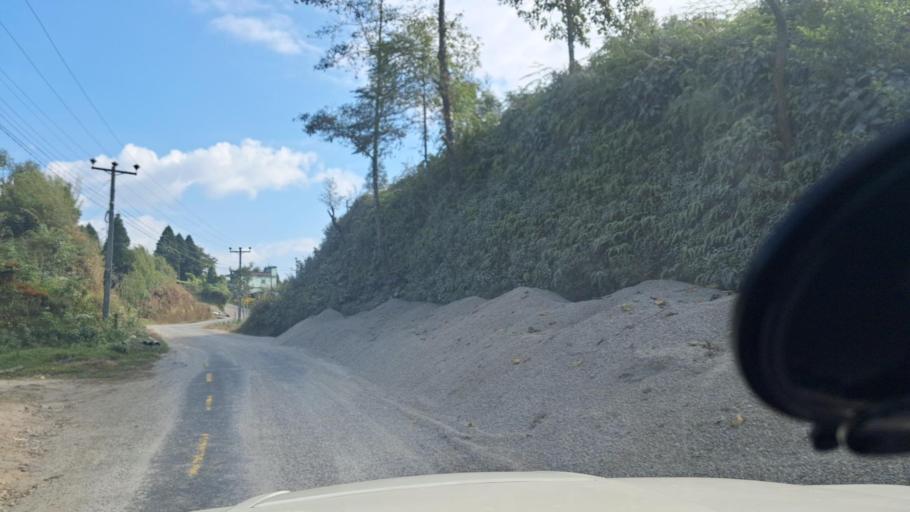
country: IN
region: West Bengal
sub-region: Darjiling
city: Mirik
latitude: 26.9152
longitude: 88.0811
